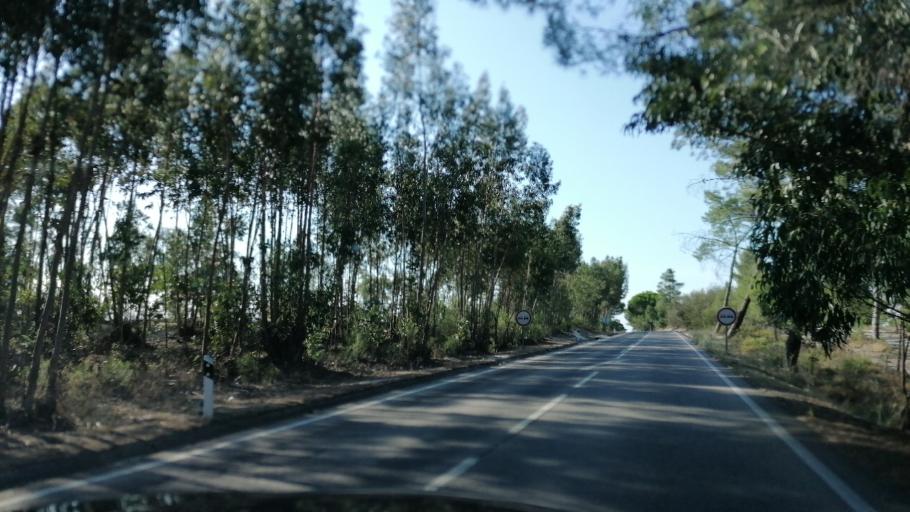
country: PT
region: Santarem
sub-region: Coruche
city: Coruche
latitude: 38.9824
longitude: -8.5469
